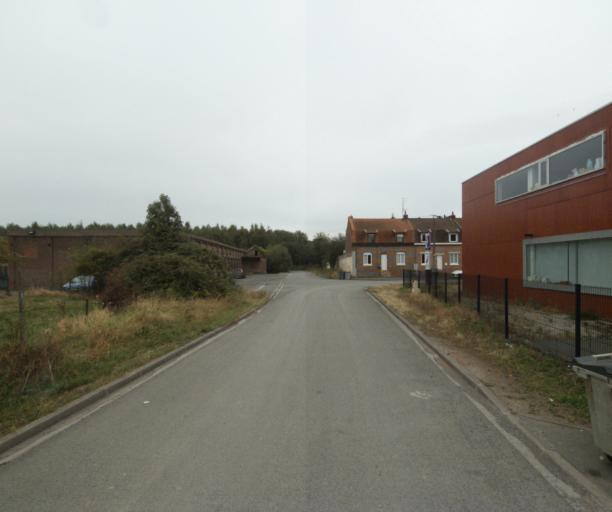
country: FR
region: Nord-Pas-de-Calais
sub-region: Departement du Nord
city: Baisieux
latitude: 50.6080
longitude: 3.2554
